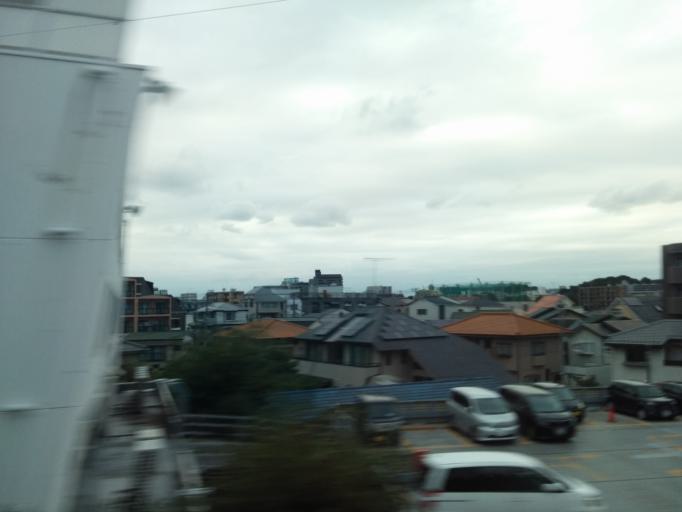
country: JP
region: Kanagawa
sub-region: Kawasaki-shi
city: Kawasaki
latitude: 35.5316
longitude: 139.6398
